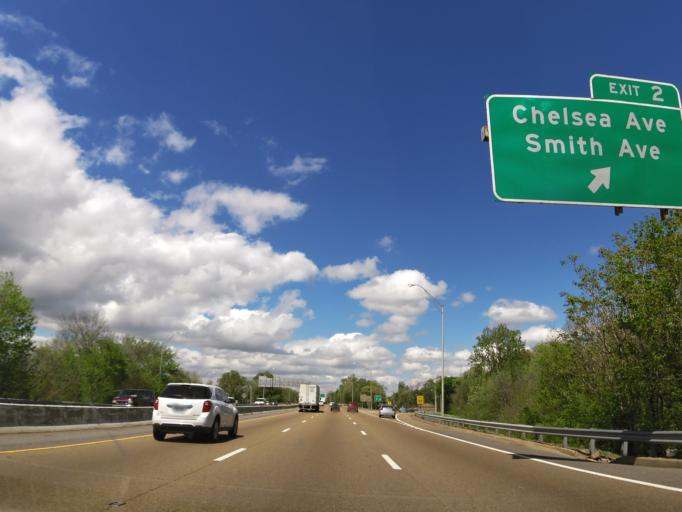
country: US
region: Tennessee
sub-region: Shelby County
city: Memphis
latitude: 35.1676
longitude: -90.0185
